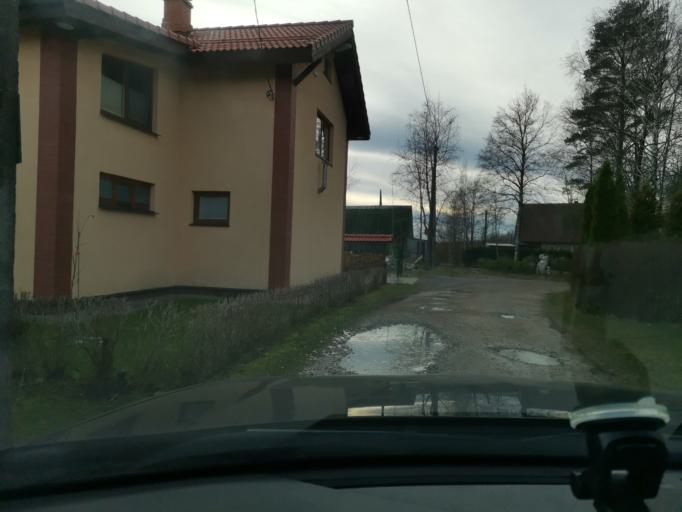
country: EE
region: Ida-Virumaa
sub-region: Sillamaee linn
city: Sillamae
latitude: 59.2534
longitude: 27.9171
